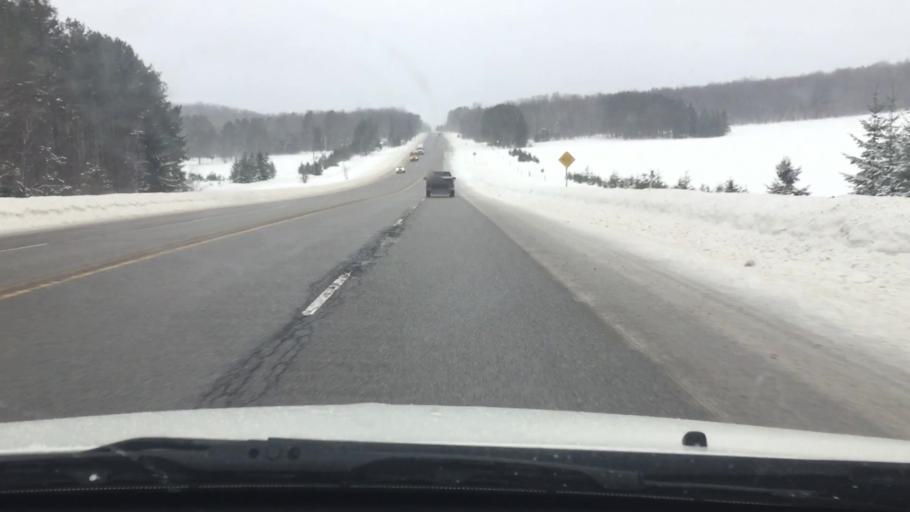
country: US
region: Michigan
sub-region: Otsego County
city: Gaylord
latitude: 45.0499
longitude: -84.7758
